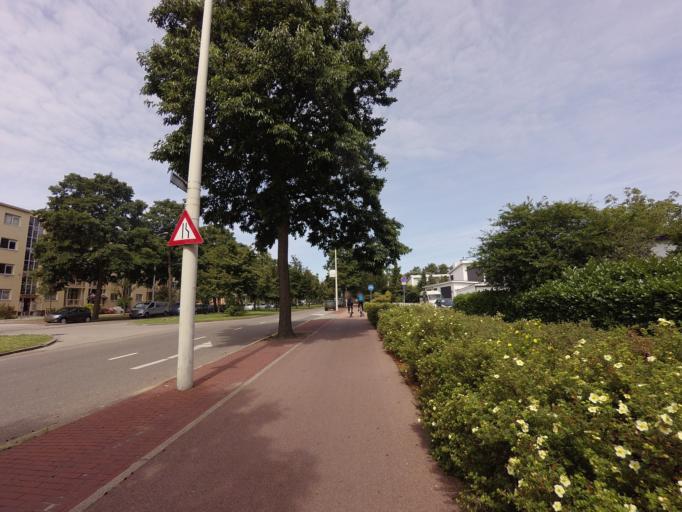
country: NL
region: South Holland
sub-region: Gemeente Den Haag
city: The Hague
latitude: 52.0531
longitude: 4.2788
